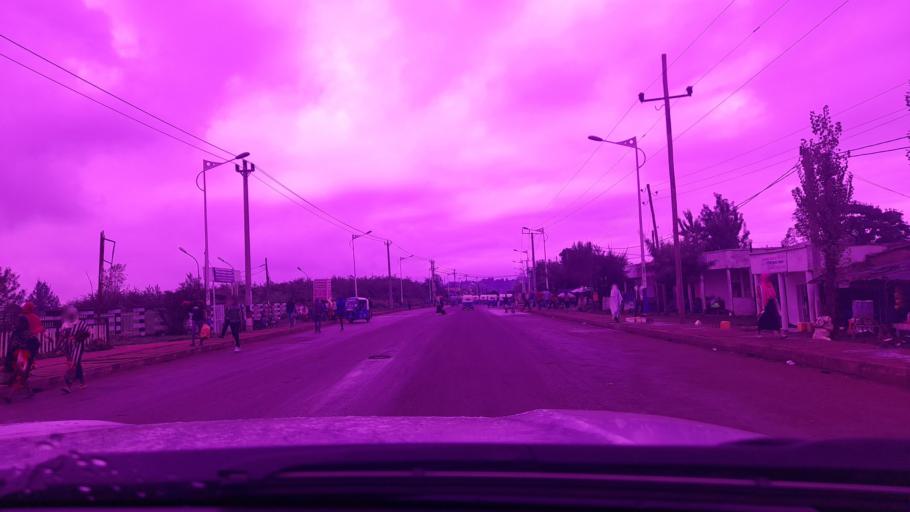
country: ET
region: Oromiya
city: Jima
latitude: 7.6569
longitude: 36.8439
